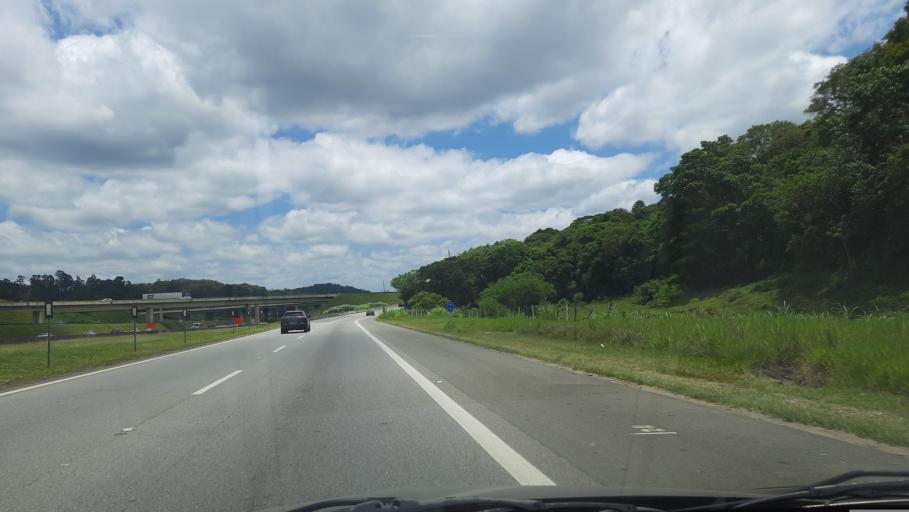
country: BR
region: Sao Paulo
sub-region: Caieiras
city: Caieiras
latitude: -23.4383
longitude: -46.7572
